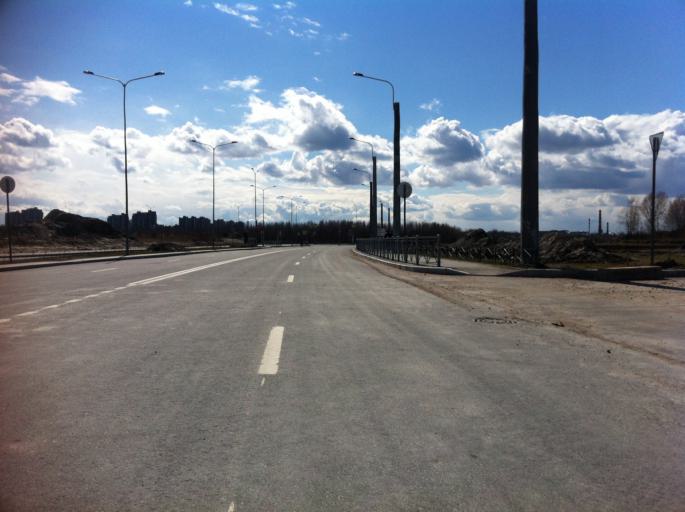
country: RU
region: St.-Petersburg
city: Sosnovaya Polyana
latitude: 59.8662
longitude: 30.1517
